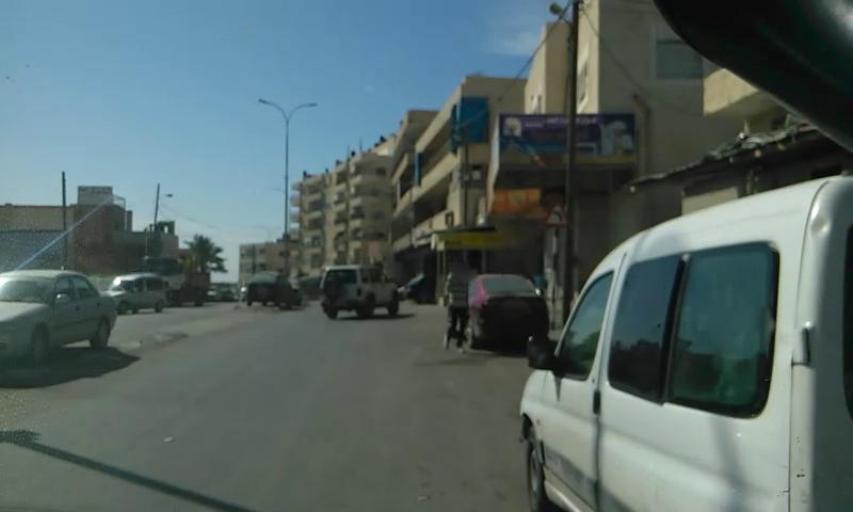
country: PS
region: West Bank
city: Al `Ayzariyah
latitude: 31.7623
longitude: 35.2813
